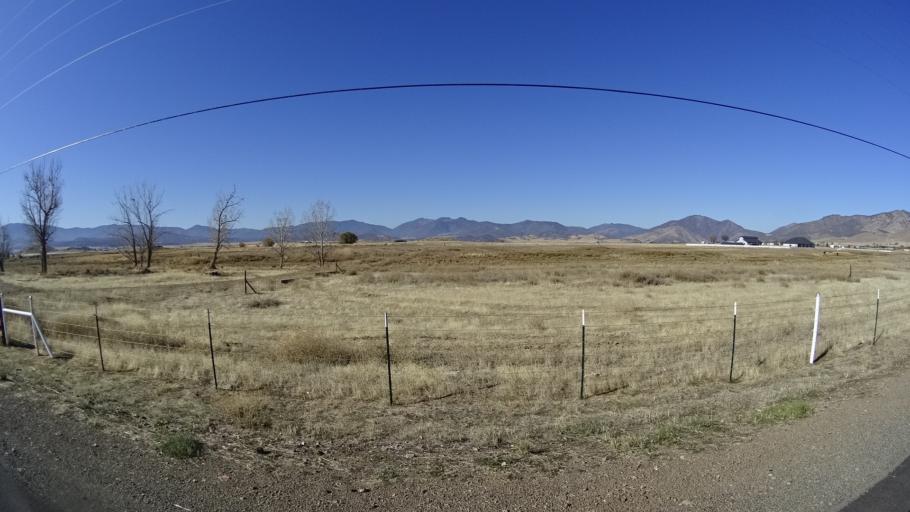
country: US
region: California
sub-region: Siskiyou County
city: Montague
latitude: 41.7455
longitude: -122.5245
